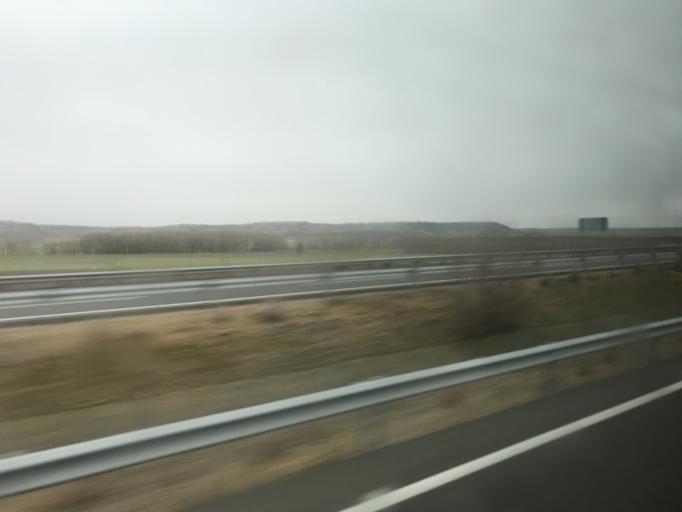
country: ES
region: Castille and Leon
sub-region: Provincia de Burgos
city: Villaverde-Mogina
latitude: 42.1667
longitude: -4.0736
